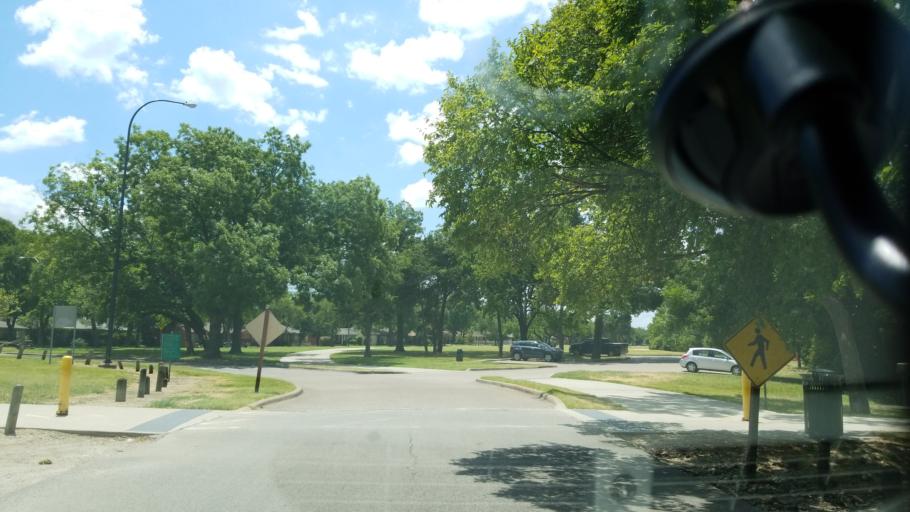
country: US
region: Texas
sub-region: Dallas County
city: Cockrell Hill
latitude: 32.7093
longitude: -96.8494
